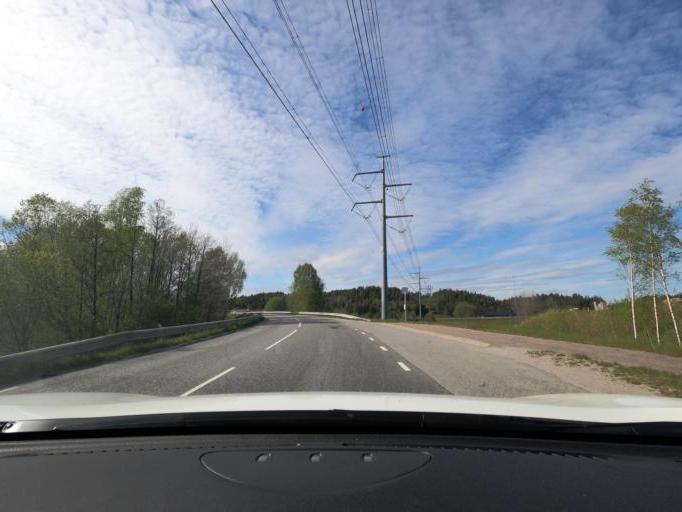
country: SE
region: Vaestra Goetaland
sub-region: Harryda Kommun
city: Landvetter
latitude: 57.6820
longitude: 12.2410
